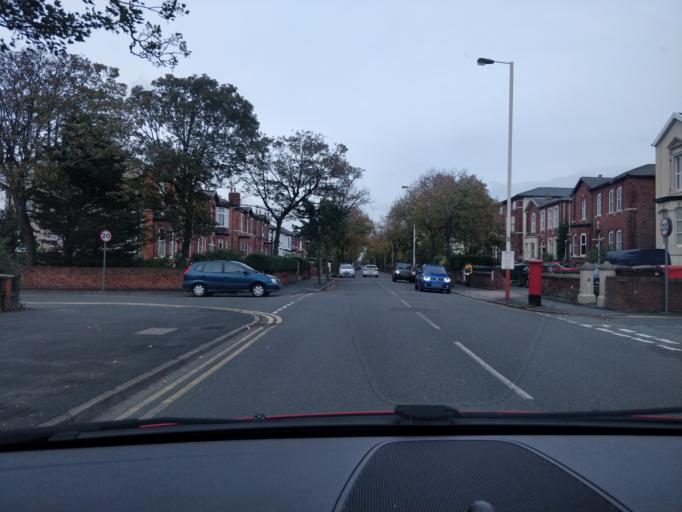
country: GB
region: England
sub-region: Sefton
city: Southport
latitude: 53.6529
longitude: -2.9973
